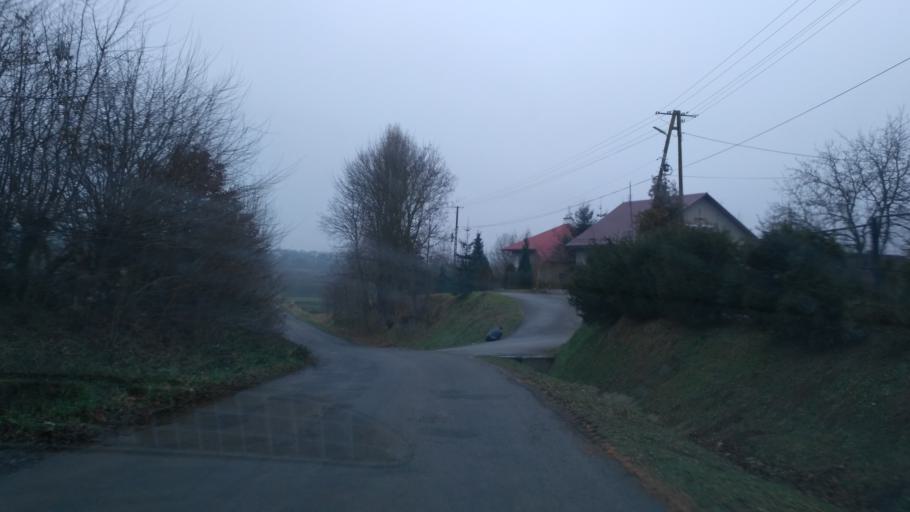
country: PL
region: Subcarpathian Voivodeship
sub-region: Powiat przeworski
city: Zarzecze
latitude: 49.9709
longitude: 22.5671
